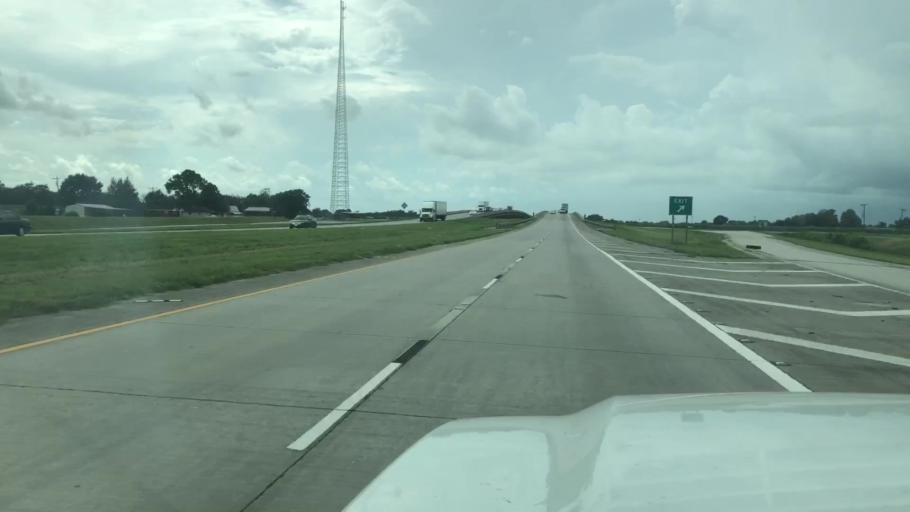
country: US
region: Louisiana
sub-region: Iberia Parish
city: Jeanerette
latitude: 29.9173
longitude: -91.7247
